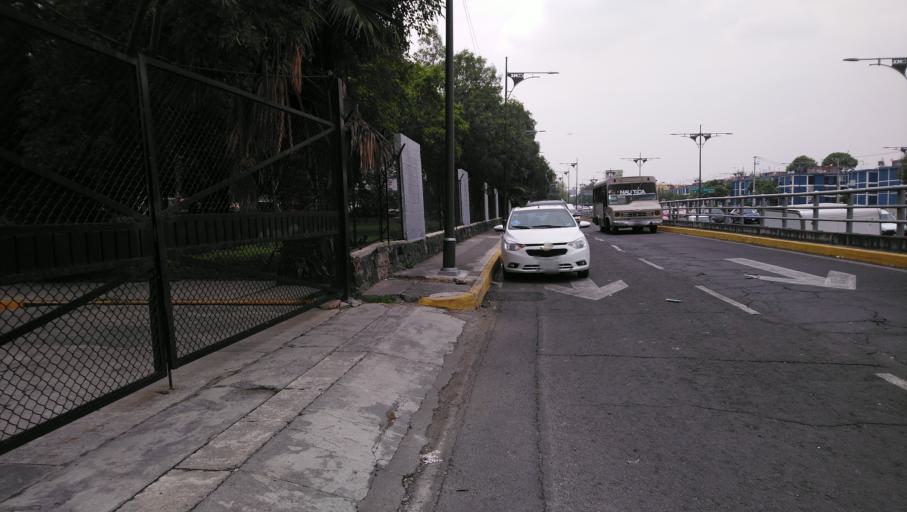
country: MX
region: Mexico City
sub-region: Iztacalco
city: Iztacalco
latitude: 19.4076
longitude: -99.1041
